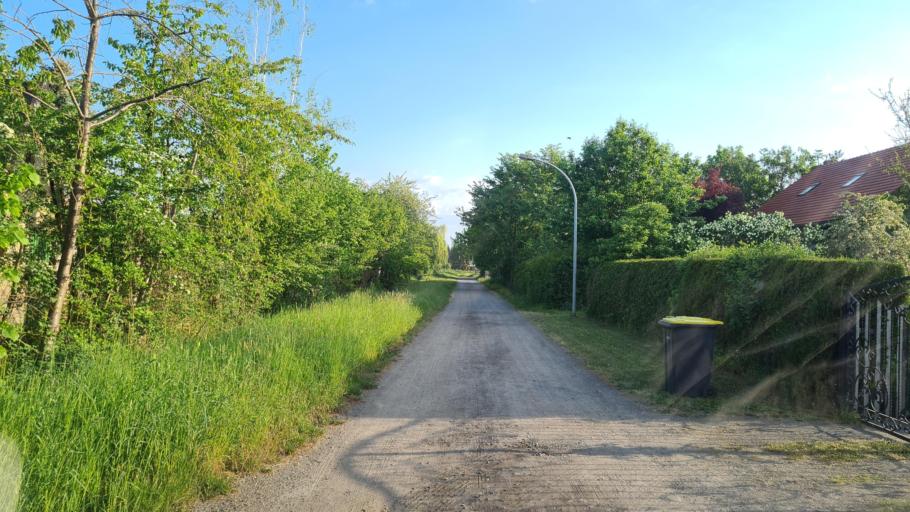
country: DE
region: Brandenburg
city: Falkenberg
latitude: 51.5828
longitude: 13.2276
